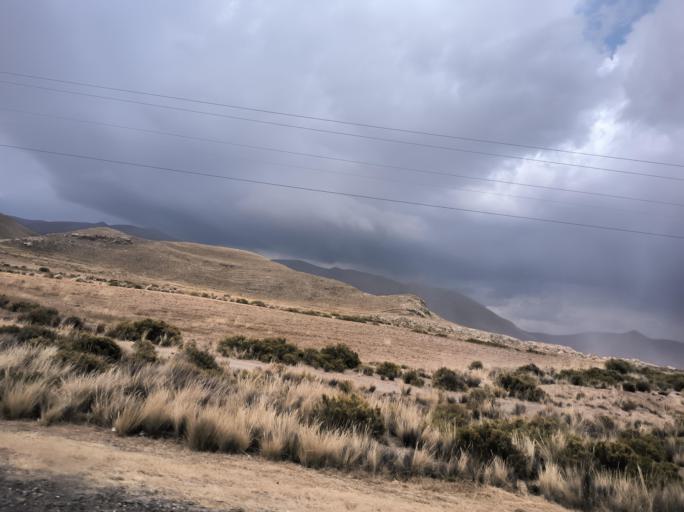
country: BO
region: Oruro
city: Challapata
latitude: -18.7547
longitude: -66.8622
